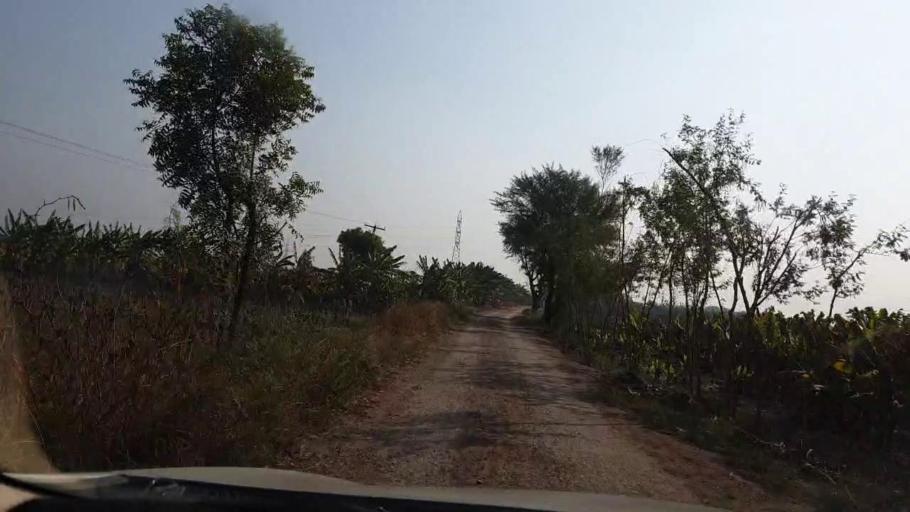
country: PK
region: Sindh
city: Matiari
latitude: 25.6370
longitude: 68.4967
